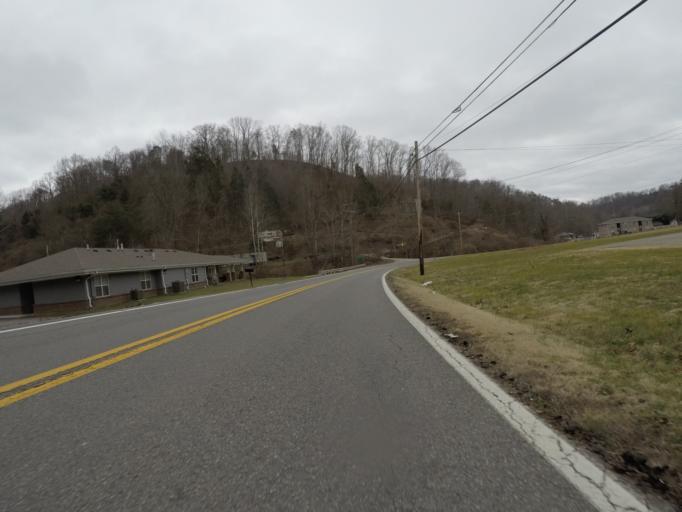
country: US
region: West Virginia
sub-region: Cabell County
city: Barboursville
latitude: 38.4391
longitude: -82.2918
